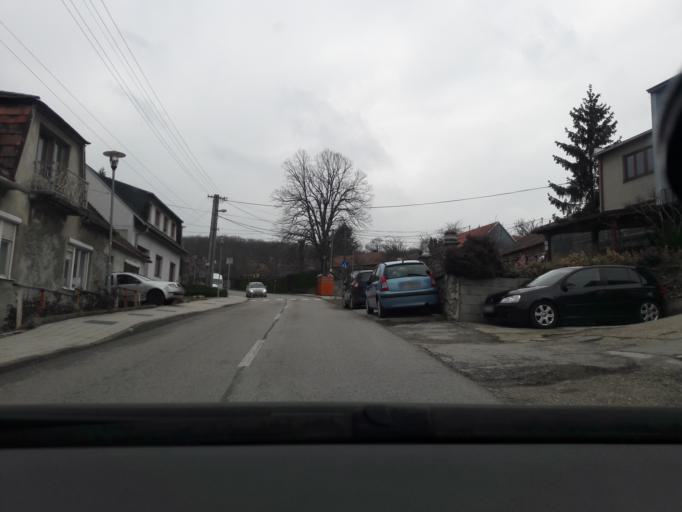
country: SK
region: Bratislavsky
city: Modra
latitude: 48.3950
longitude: 17.3497
